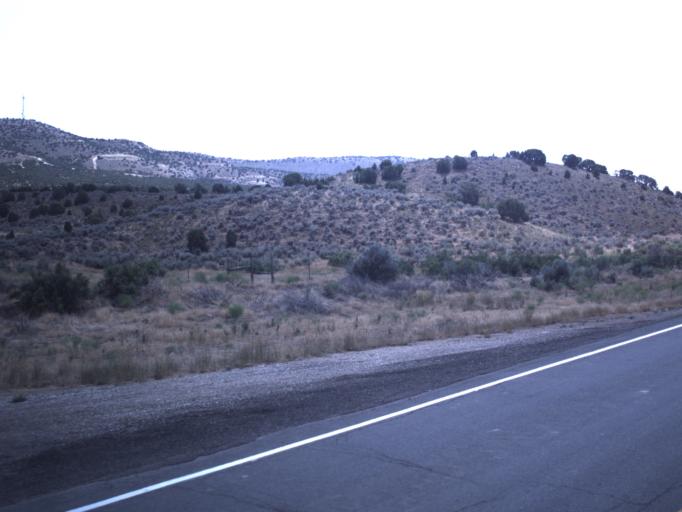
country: US
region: Utah
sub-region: Uintah County
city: Maeser
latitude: 40.4574
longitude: -109.6171
